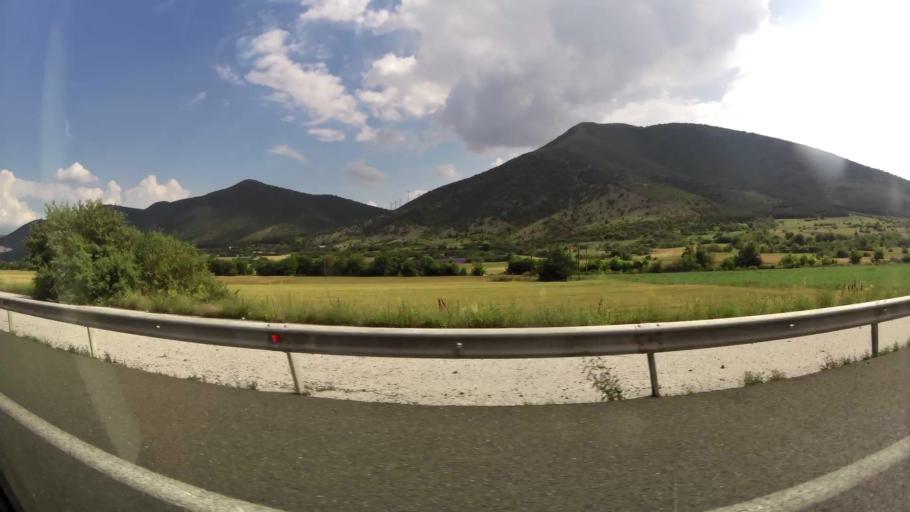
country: GR
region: West Macedonia
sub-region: Nomos Kozanis
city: Akrini
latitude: 40.3681
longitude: 21.9064
